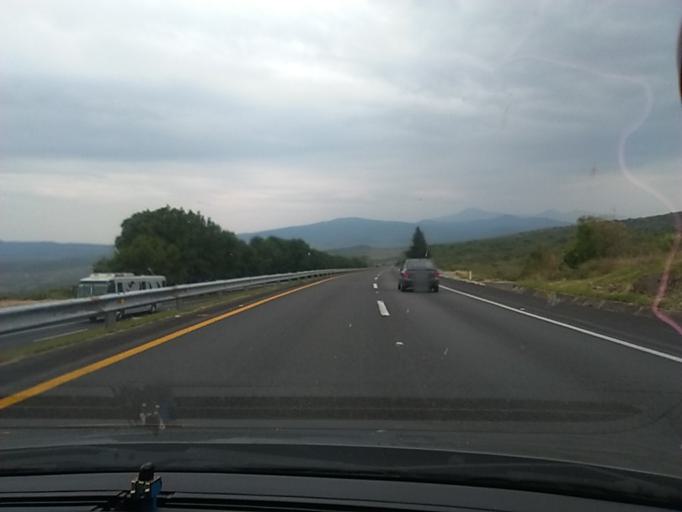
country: MX
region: Michoacan
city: Penjamillo de Degollado
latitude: 20.0701
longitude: -101.9669
